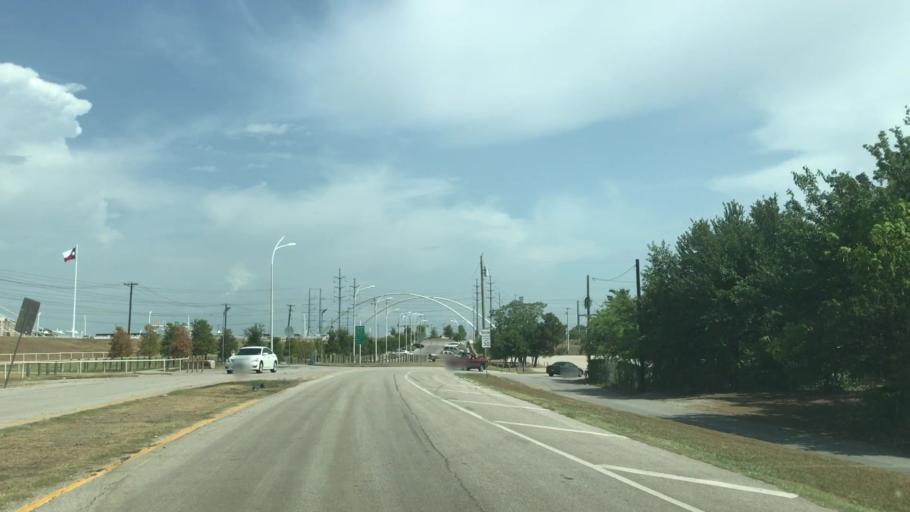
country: US
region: Texas
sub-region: Dallas County
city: Dallas
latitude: 32.7817
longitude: -96.8281
